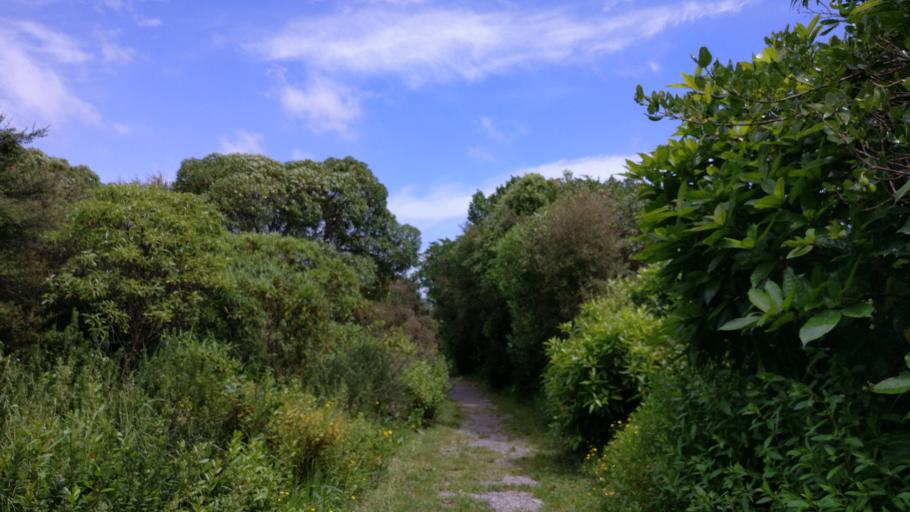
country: NZ
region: Wellington
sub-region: Porirua City
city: Porirua
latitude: -41.1031
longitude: 174.9163
